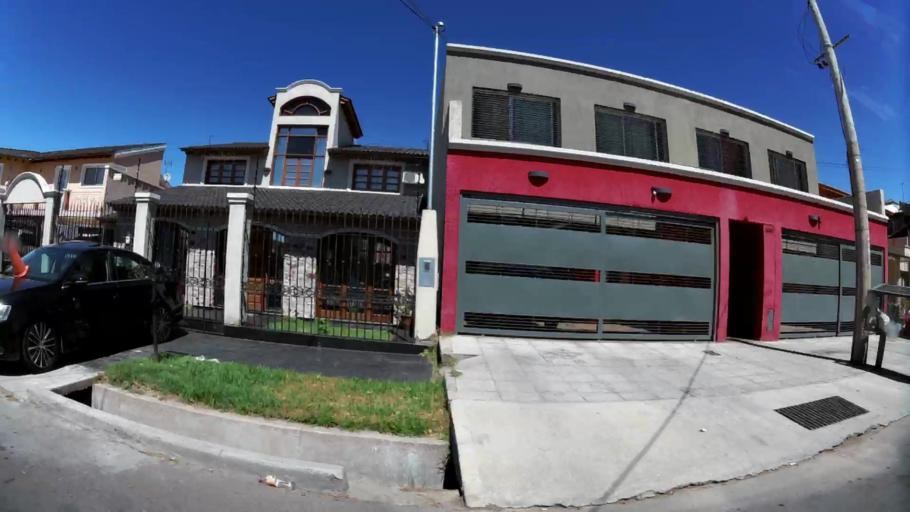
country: AR
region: Mendoza
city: Las Heras
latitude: -32.8529
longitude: -68.8545
